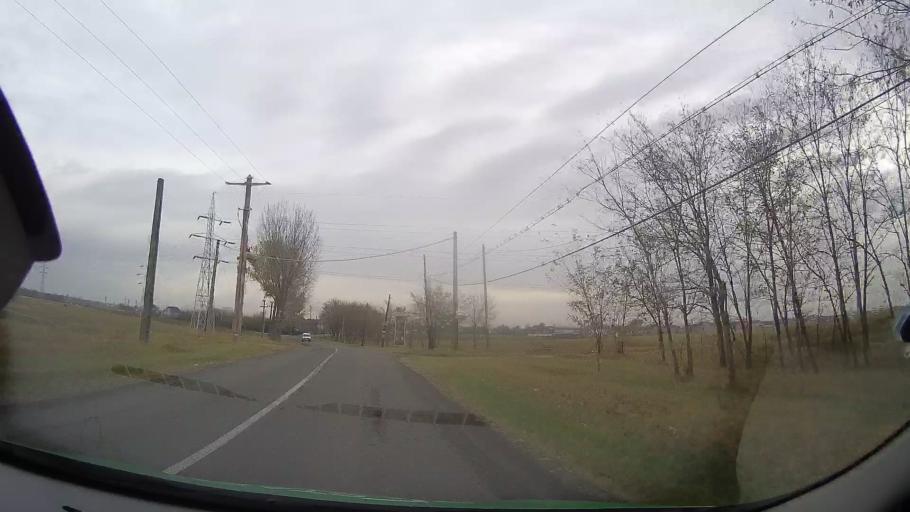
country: RO
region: Prahova
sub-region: Comuna Berceni
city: Berceni
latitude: 44.9381
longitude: 26.1153
